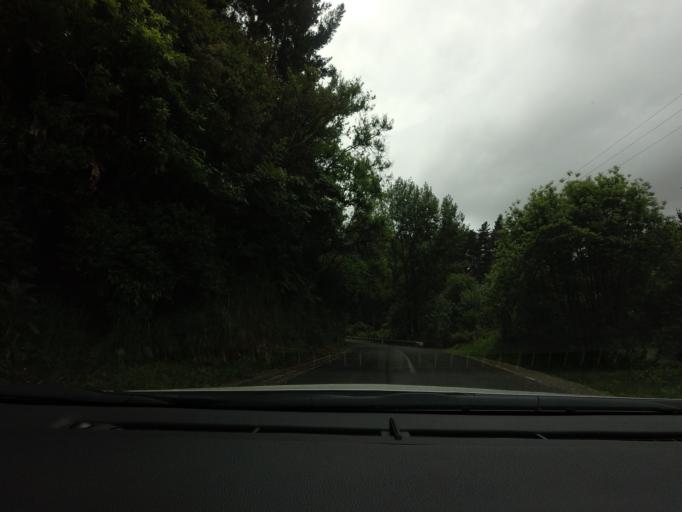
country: NZ
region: Auckland
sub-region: Auckland
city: Warkworth
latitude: -36.5001
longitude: 174.6277
